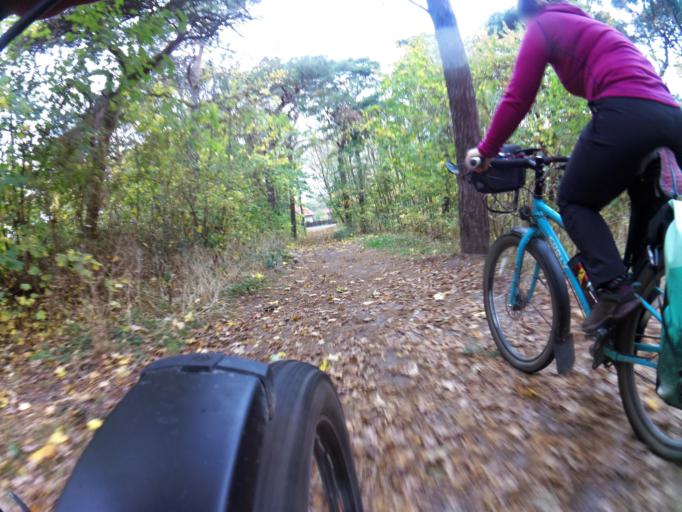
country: PL
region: Pomeranian Voivodeship
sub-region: Powiat pucki
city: Jastarnia
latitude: 54.6975
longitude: 18.6873
